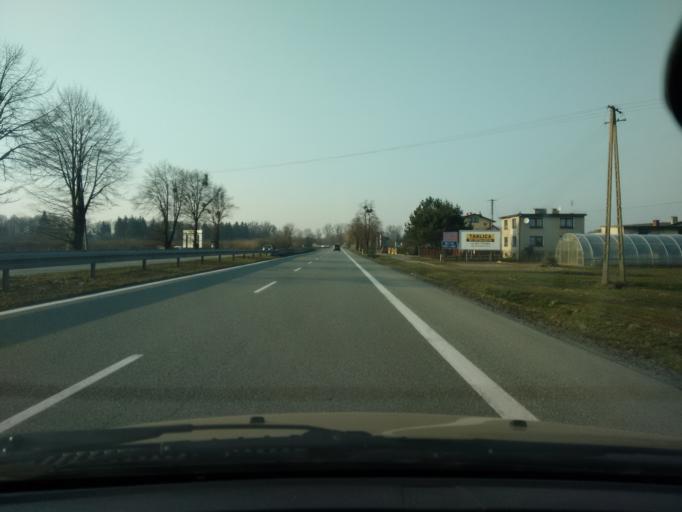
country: PL
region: Silesian Voivodeship
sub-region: Powiat cieszynski
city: Drogomysl
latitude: 49.8943
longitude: 18.7458
